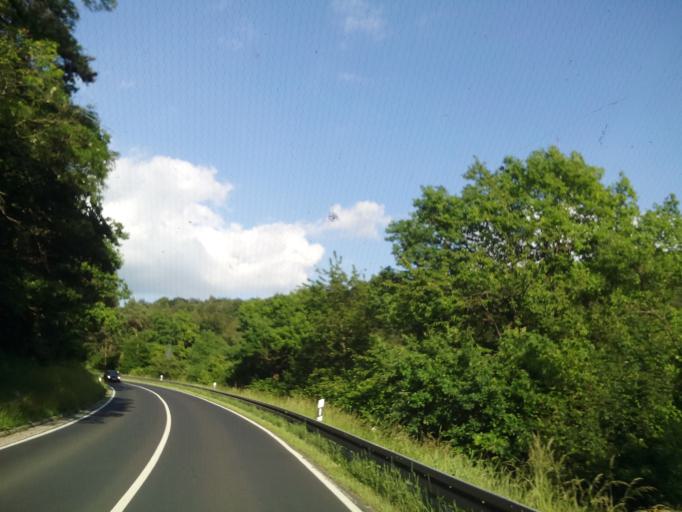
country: DE
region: Bavaria
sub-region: Regierungsbezirk Unterfranken
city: Nudlingen
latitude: 50.2237
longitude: 10.1478
